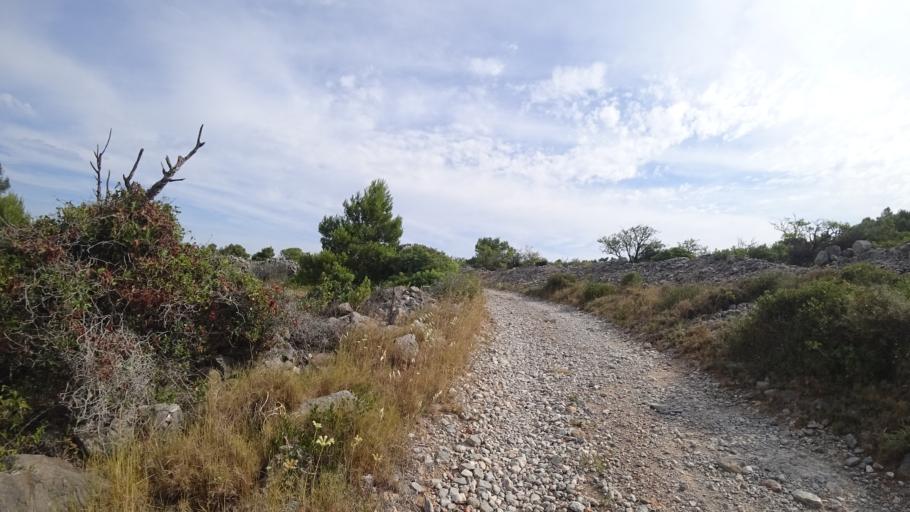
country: FR
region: Languedoc-Roussillon
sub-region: Departement de l'Aude
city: Leucate
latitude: 42.9009
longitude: 3.0247
